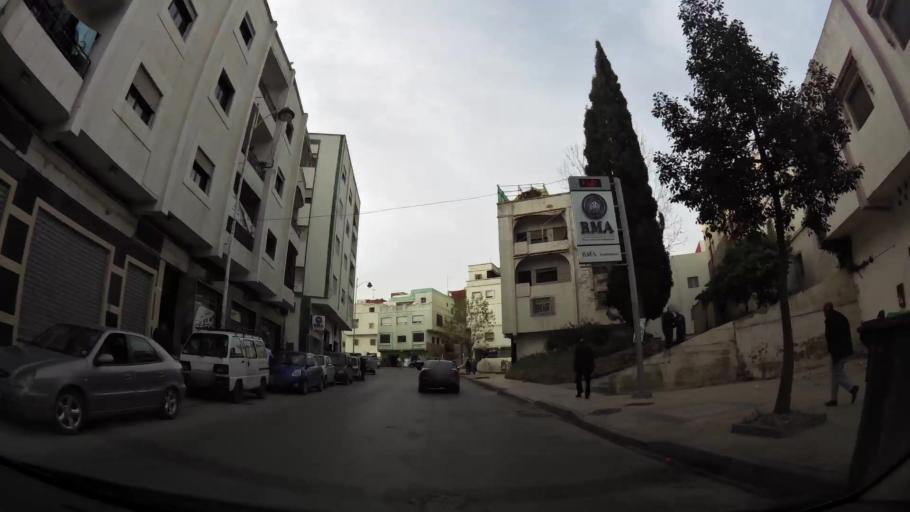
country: MA
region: Tanger-Tetouan
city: Tetouan
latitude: 35.5671
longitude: -5.3607
